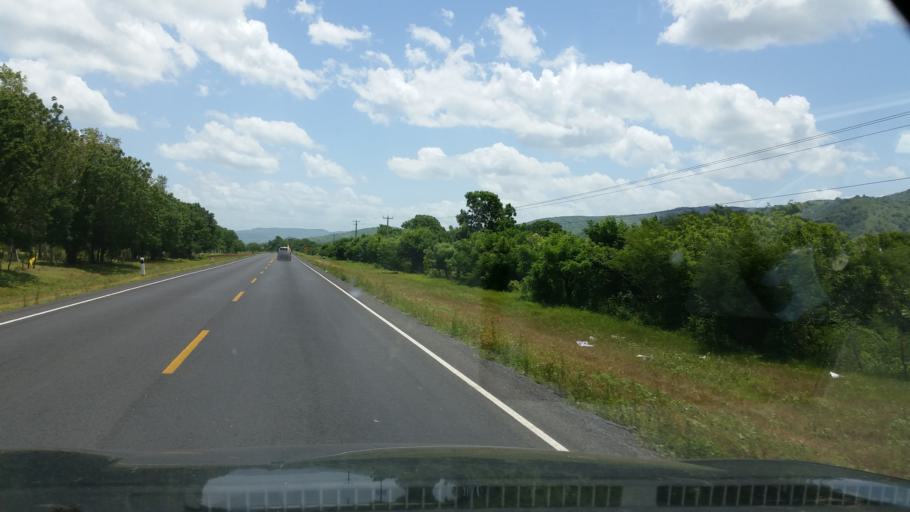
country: NI
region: Managua
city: Tipitapa
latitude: 12.3968
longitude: -86.0435
